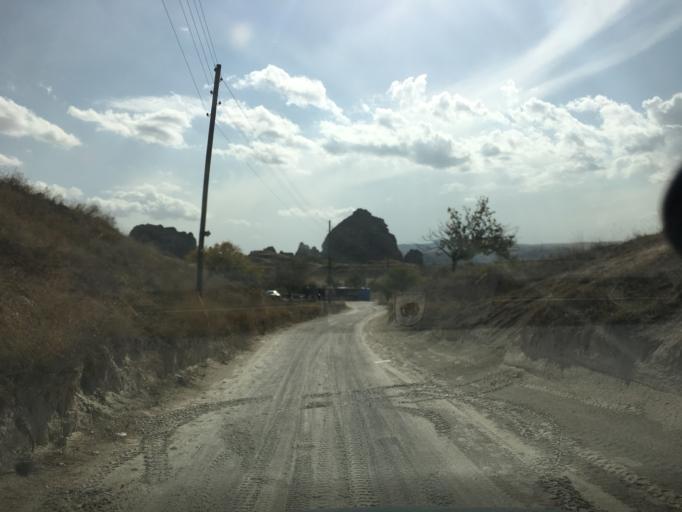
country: TR
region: Nevsehir
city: Goereme
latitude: 38.6633
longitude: 34.8413
